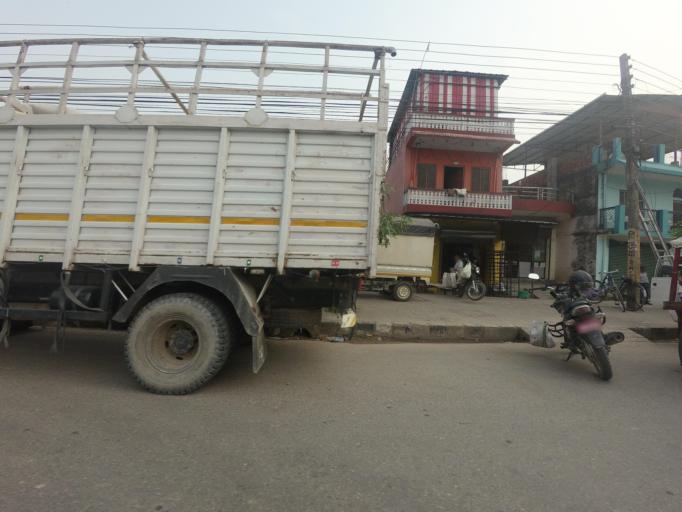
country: NP
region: Western Region
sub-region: Lumbini Zone
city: Bhairahawa
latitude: 27.5086
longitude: 83.4313
